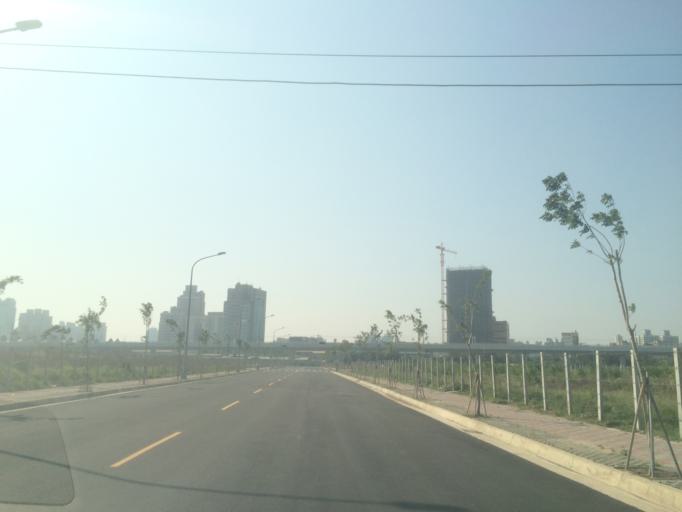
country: TW
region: Taiwan
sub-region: Taichung City
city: Taichung
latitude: 24.1760
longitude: 120.7052
